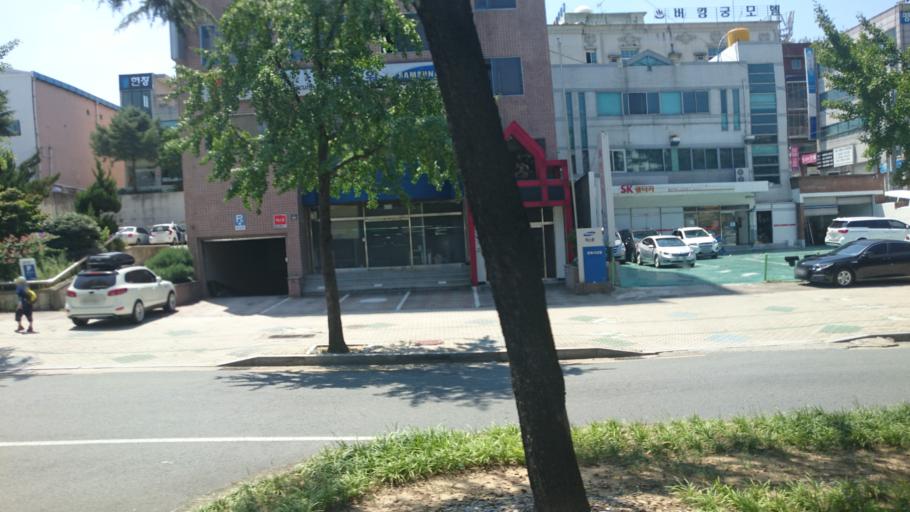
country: KR
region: Daegu
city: Daegu
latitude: 35.8825
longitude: 128.6245
